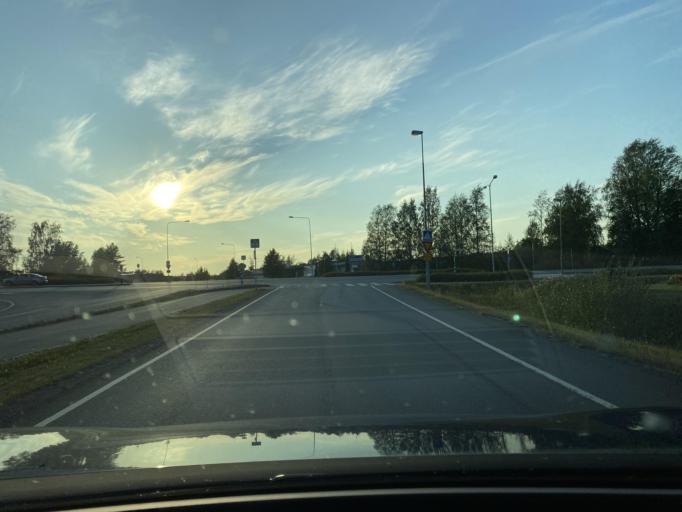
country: FI
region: Southern Ostrobothnia
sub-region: Seinaejoki
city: Nurmo
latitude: 62.8087
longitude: 22.8798
